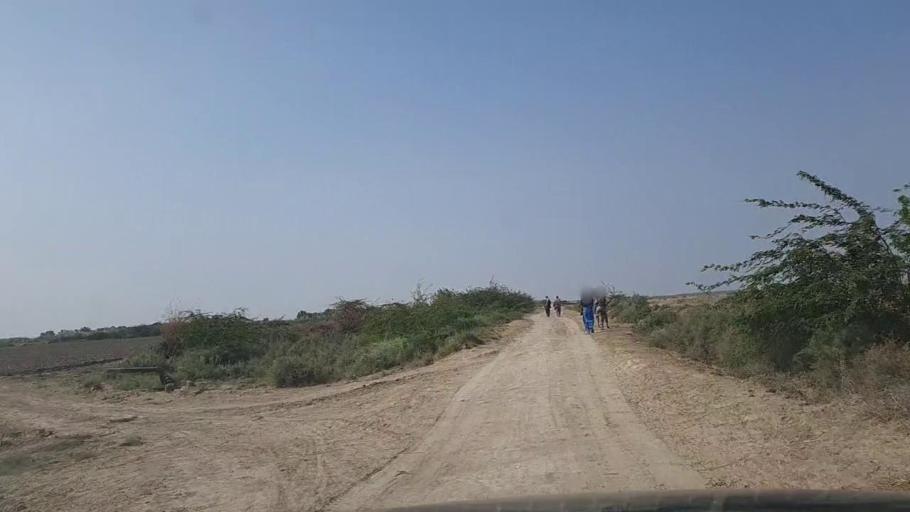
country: PK
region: Sindh
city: Gharo
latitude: 24.7046
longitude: 67.5779
